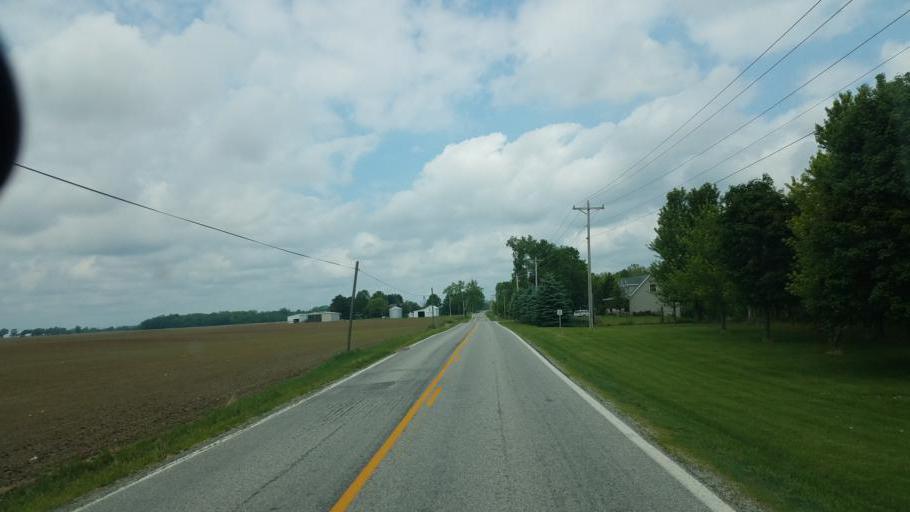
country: US
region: Ohio
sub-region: Marion County
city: Prospect
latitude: 40.4024
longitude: -83.1972
